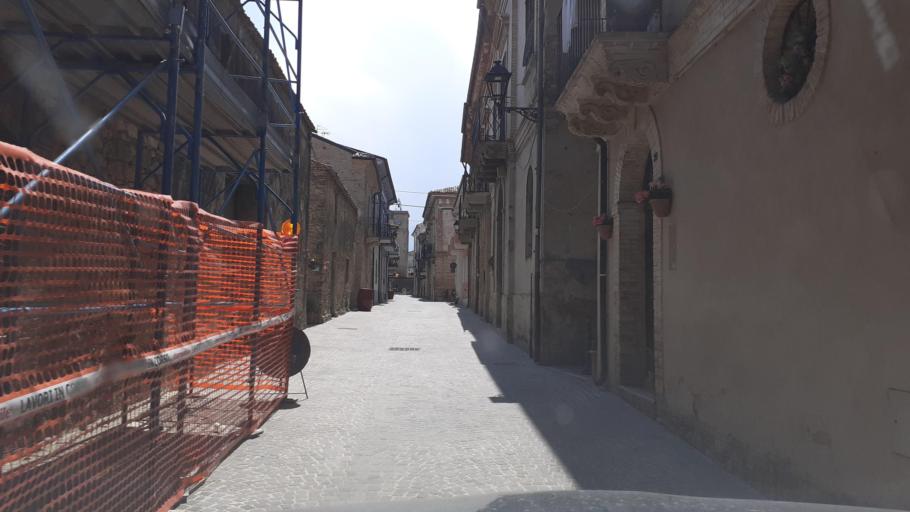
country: IT
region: Abruzzo
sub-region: Provincia di Chieti
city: Rocca San Giovanni
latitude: 42.2519
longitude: 14.4661
